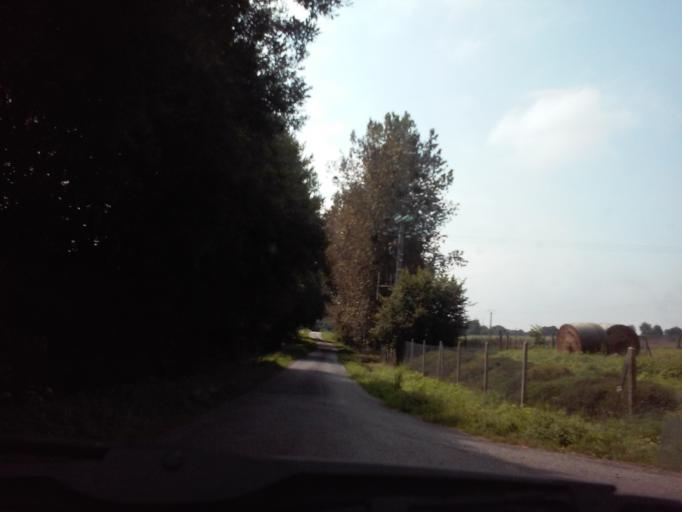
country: FR
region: Brittany
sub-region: Departement du Morbihan
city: Ploermel
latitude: 47.8979
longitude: -2.4094
